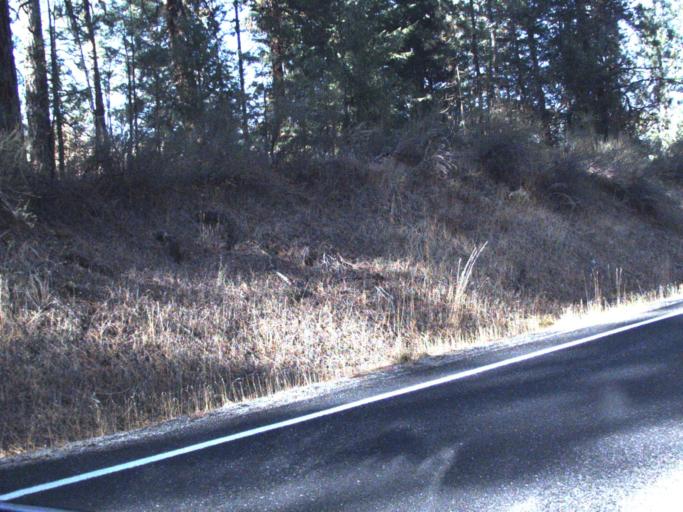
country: US
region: Washington
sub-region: Stevens County
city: Kettle Falls
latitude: 48.2165
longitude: -118.1765
